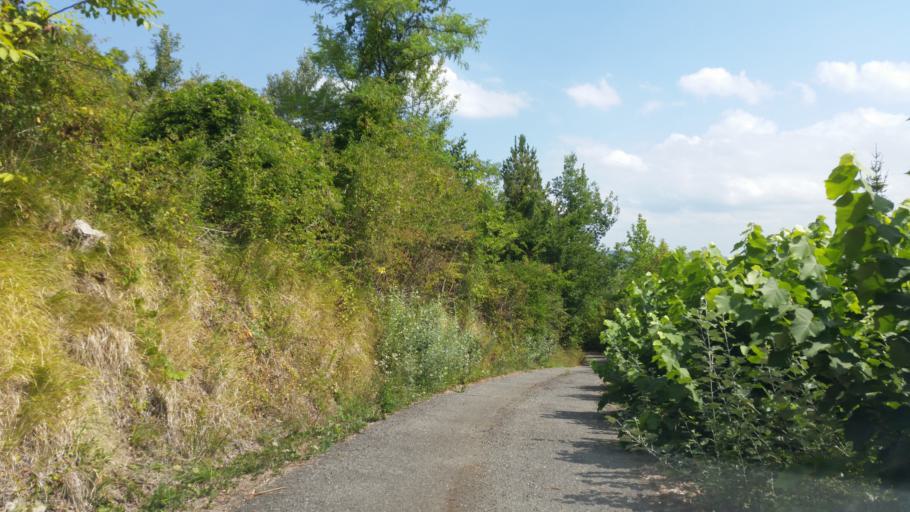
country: IT
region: Piedmont
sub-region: Provincia di Asti
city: Bubbio
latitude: 44.6319
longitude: 8.2896
